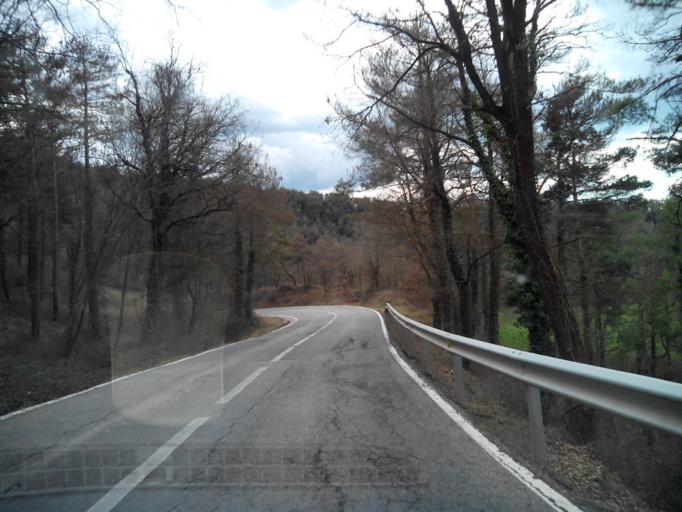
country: ES
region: Catalonia
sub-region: Provincia de Barcelona
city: Olost
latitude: 41.9695
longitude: 2.1377
